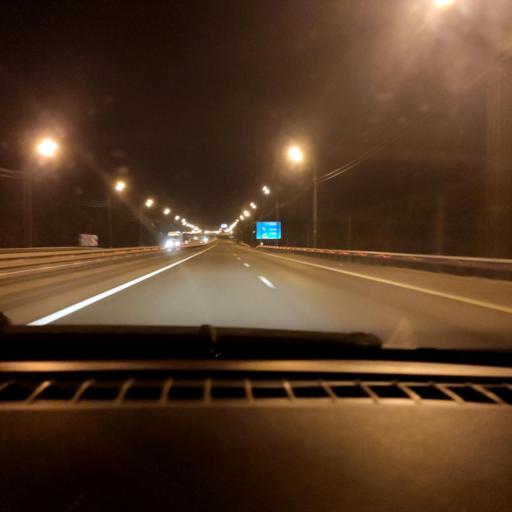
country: RU
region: Lipetsk
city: Khlevnoye
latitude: 52.2069
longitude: 39.1577
